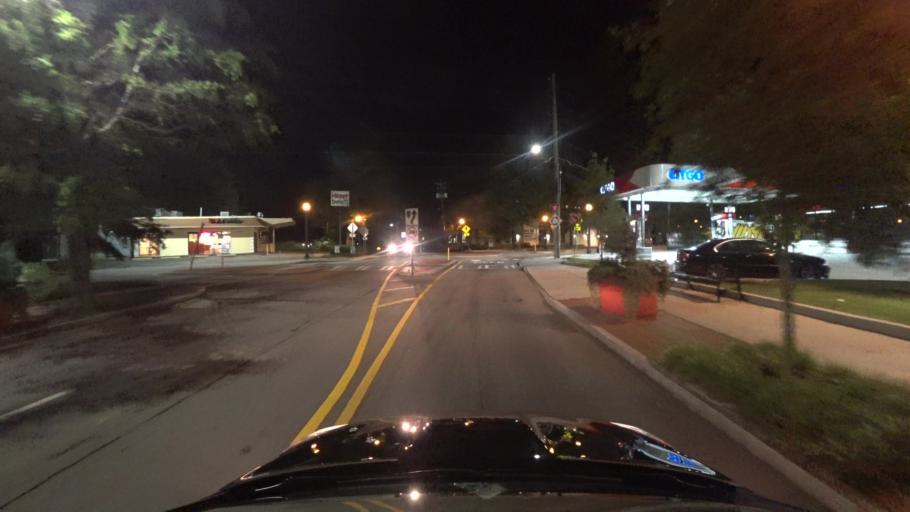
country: US
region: Georgia
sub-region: DeKalb County
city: Druid Hills
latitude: 33.7433
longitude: -84.3490
